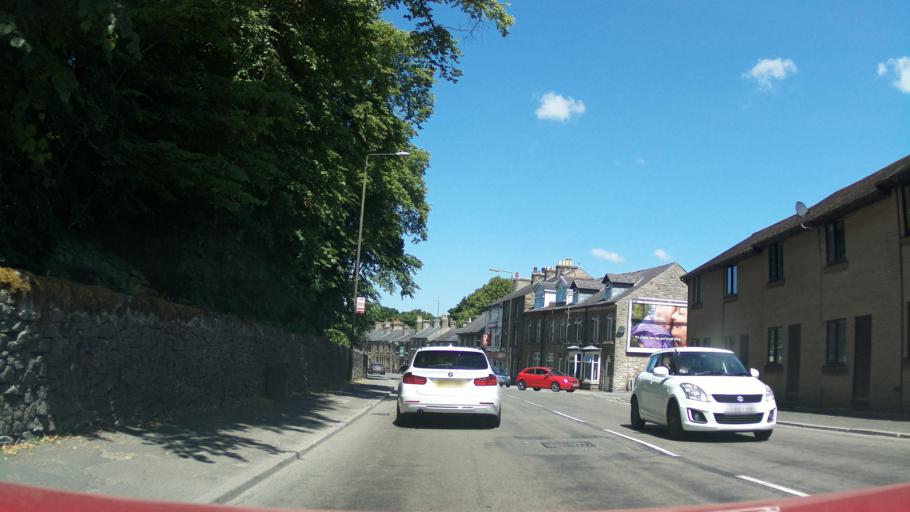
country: GB
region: England
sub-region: Derbyshire
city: Buxton
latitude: 53.2506
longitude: -1.9112
